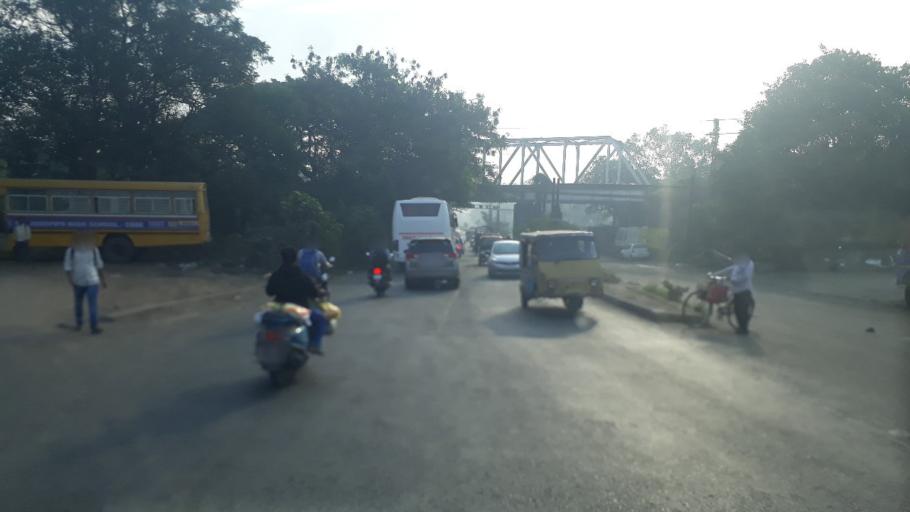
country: IN
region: Maharashtra
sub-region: Raigarh
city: Kalundri
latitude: 18.9751
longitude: 73.1229
